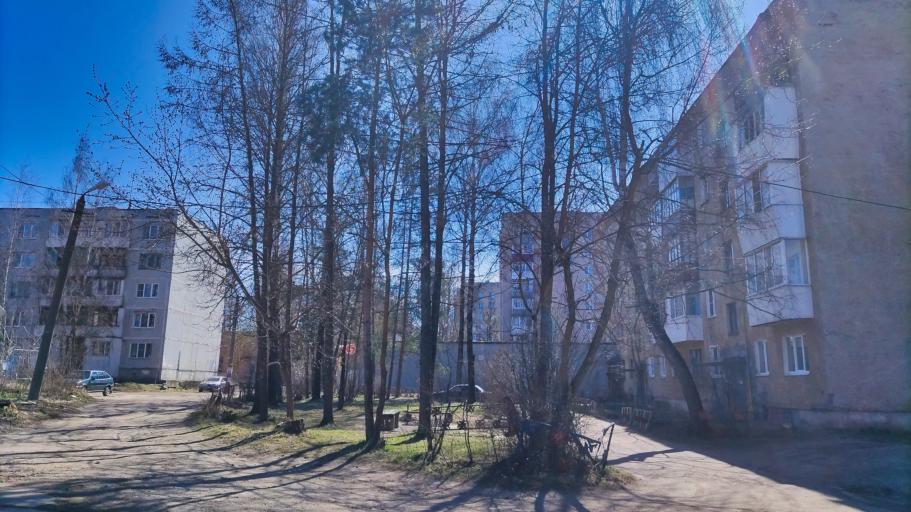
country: RU
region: Tverskaya
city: Rzhev
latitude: 56.2608
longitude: 34.3450
